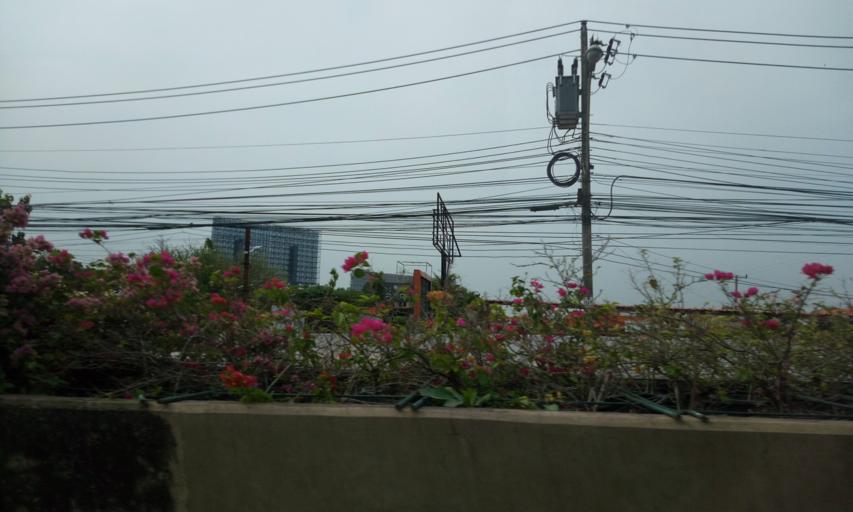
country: TH
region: Bangkok
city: Lat Krabang
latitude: 13.7216
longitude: 100.7615
